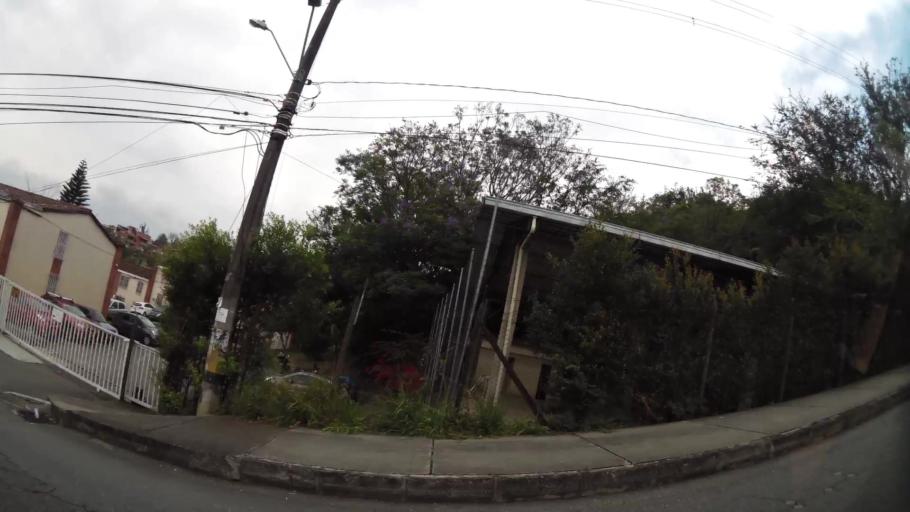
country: CO
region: Antioquia
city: Medellin
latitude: 6.2844
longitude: -75.5982
